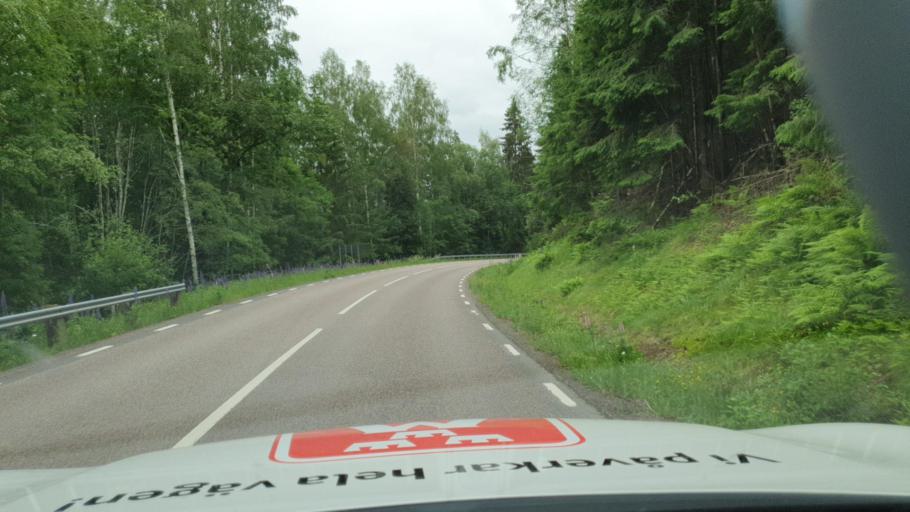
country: SE
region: Vaermland
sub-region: Sunne Kommun
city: Sunne
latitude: 59.8282
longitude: 12.9833
